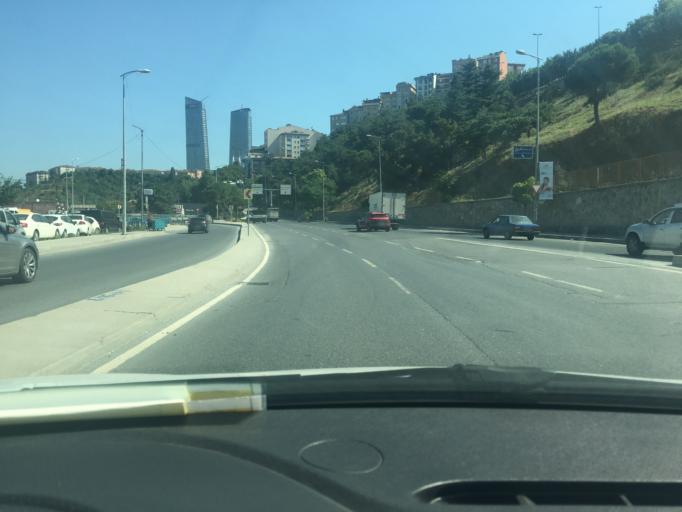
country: TR
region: Istanbul
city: Sisli
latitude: 41.0900
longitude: 28.9848
